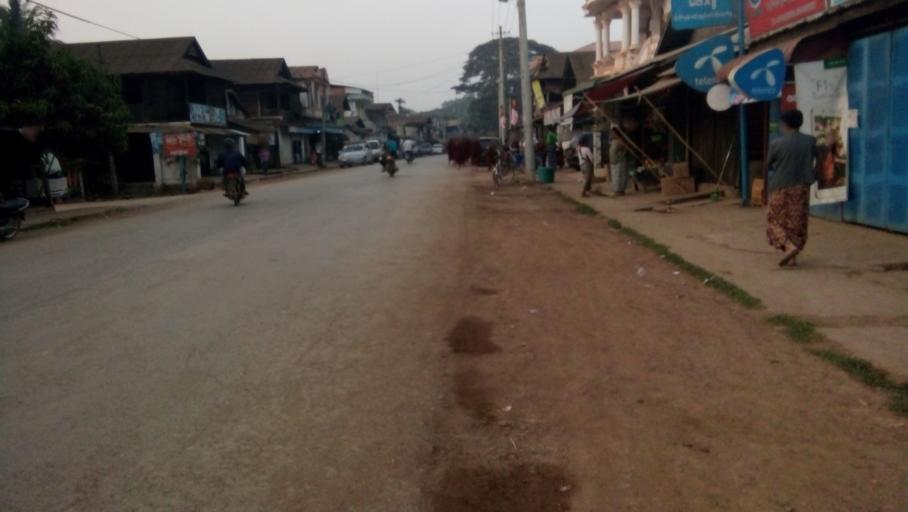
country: MM
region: Kayin
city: Hpa-an
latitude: 17.1225
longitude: 97.8193
